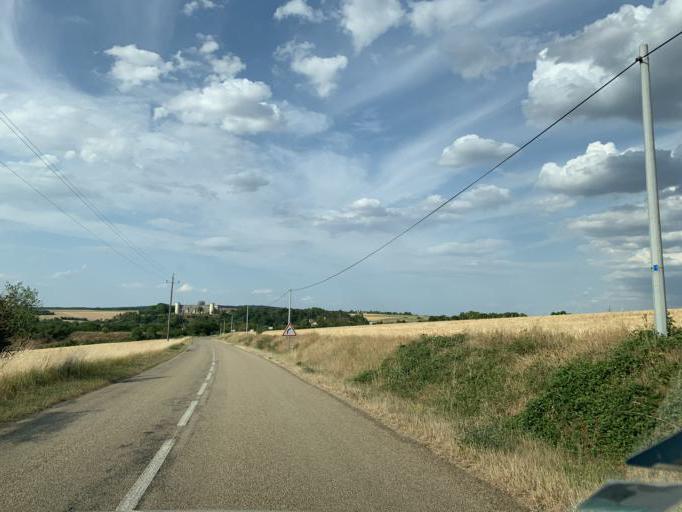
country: FR
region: Bourgogne
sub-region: Departement de l'Yonne
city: Fontenailles
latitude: 47.5416
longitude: 3.4173
